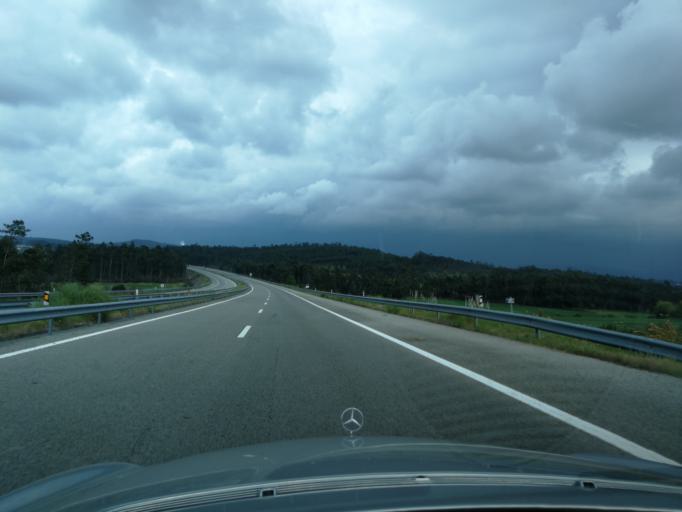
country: PT
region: Braga
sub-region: Vila Nova de Famalicao
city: Ribeirao
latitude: 41.3822
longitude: -8.6358
